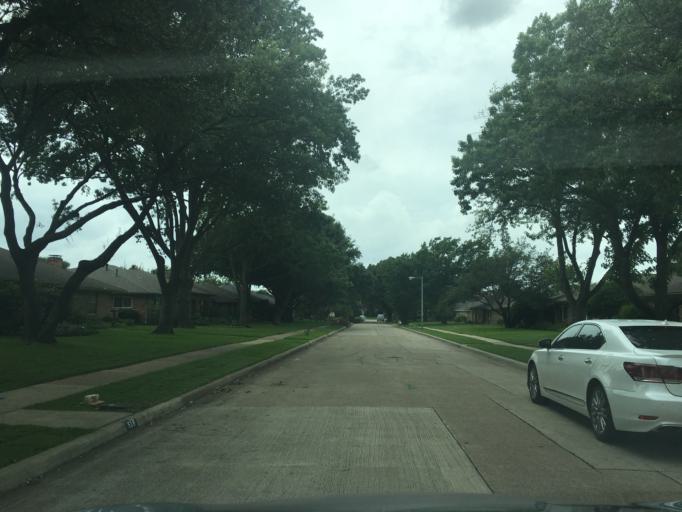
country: US
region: Texas
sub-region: Dallas County
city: Richardson
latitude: 32.9312
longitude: -96.7254
